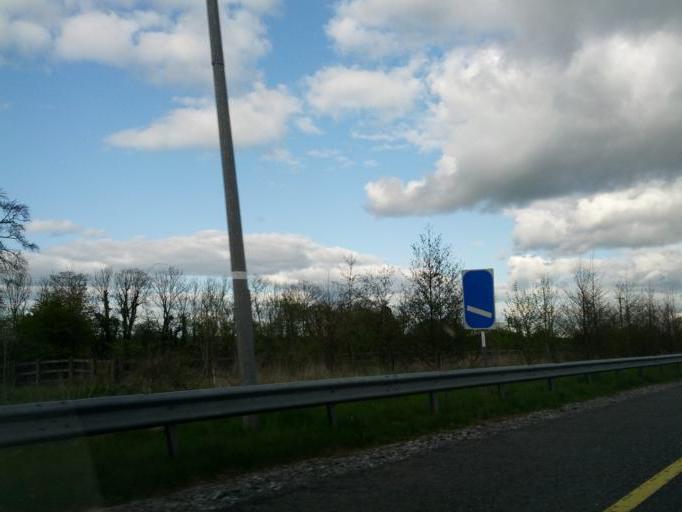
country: IE
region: Leinster
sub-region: An Iarmhi
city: Kilbeggan
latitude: 53.3594
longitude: -7.5060
